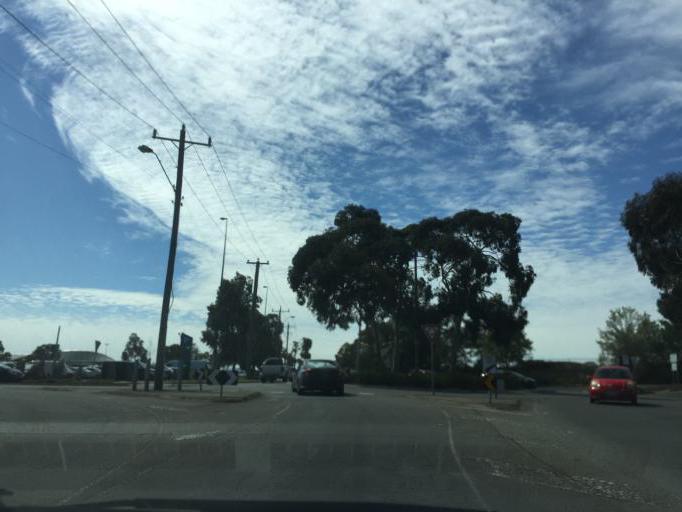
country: AU
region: Victoria
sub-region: Maribyrnong
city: Maribyrnong
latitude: -37.7758
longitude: 144.8912
